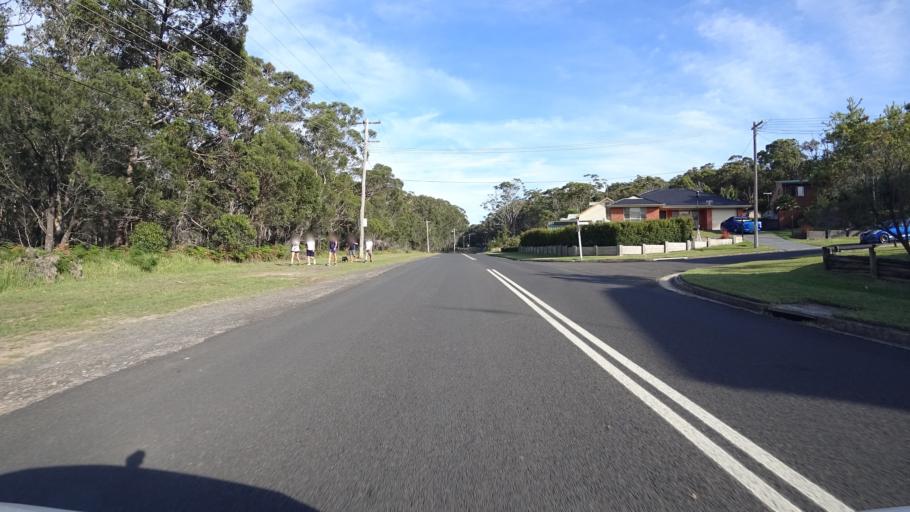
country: AU
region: New South Wales
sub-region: Shoalhaven Shire
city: Milton
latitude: -35.2630
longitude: 150.5079
